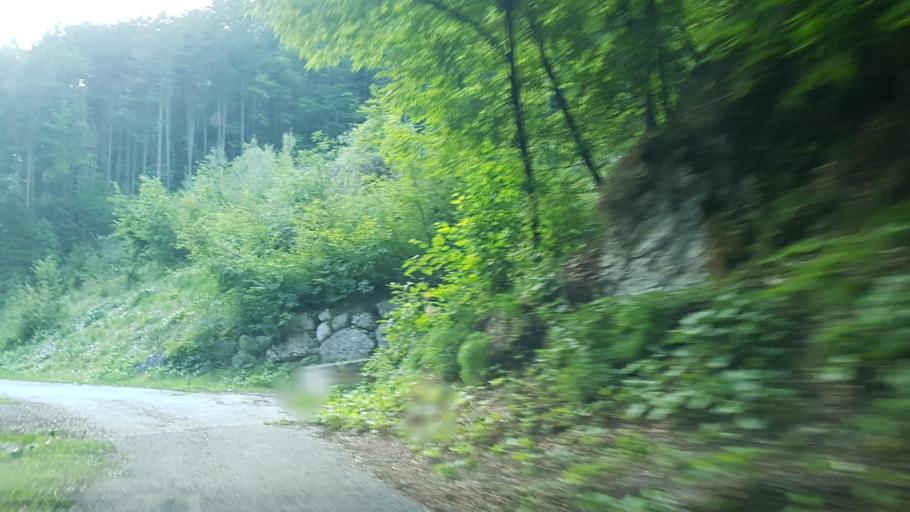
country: IT
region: Friuli Venezia Giulia
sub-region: Provincia di Udine
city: Malborghetto
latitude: 46.3976
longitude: 13.4377
